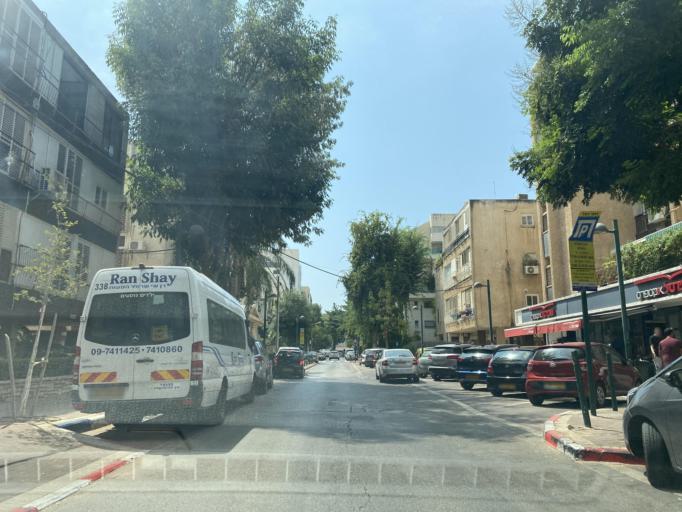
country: IL
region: Central District
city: Kfar Saba
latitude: 32.1723
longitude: 34.9045
